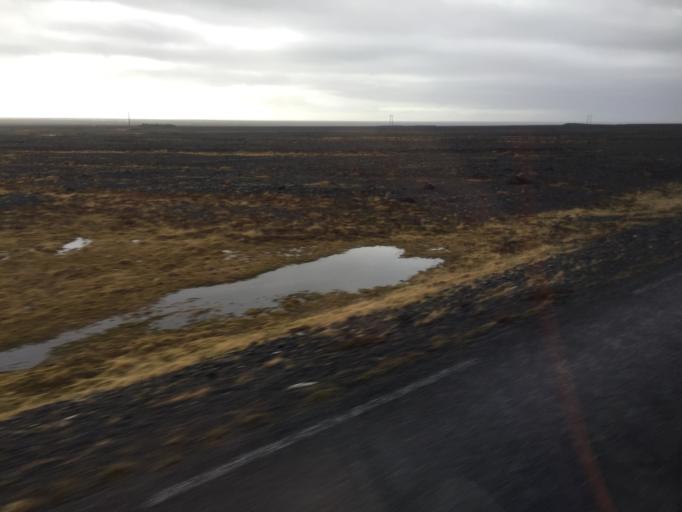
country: IS
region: East
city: Hoefn
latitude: 63.9187
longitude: -16.7689
